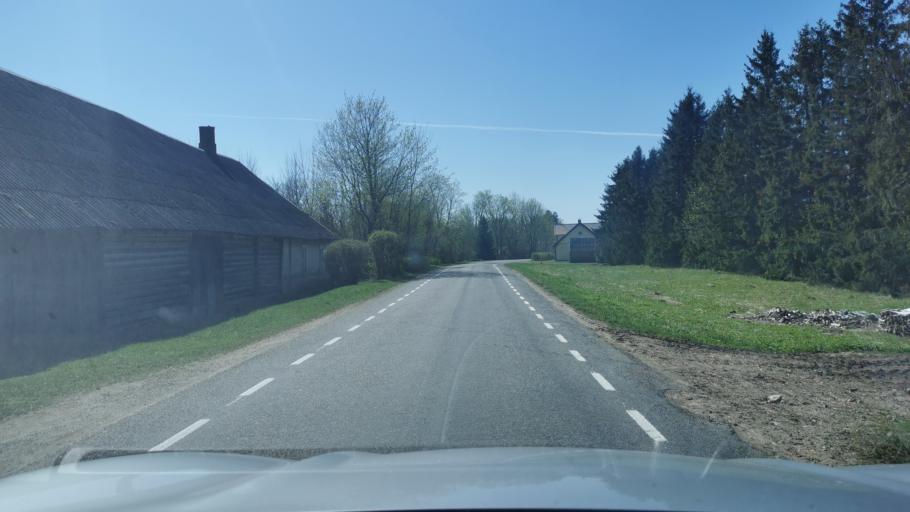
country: EE
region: Laeaene-Virumaa
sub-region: Vinni vald
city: Vinni
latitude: 59.0965
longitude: 26.6164
